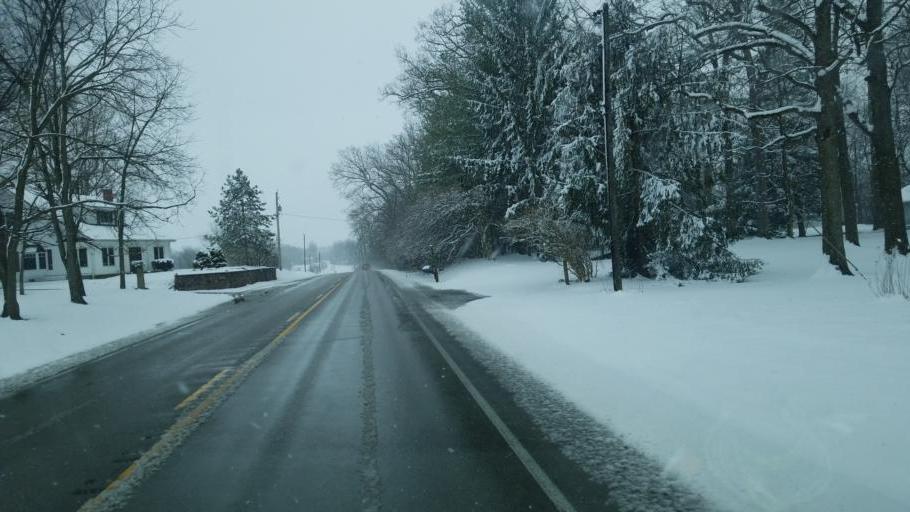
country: US
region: Indiana
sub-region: Delaware County
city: Muncie
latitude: 40.0933
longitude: -85.3132
